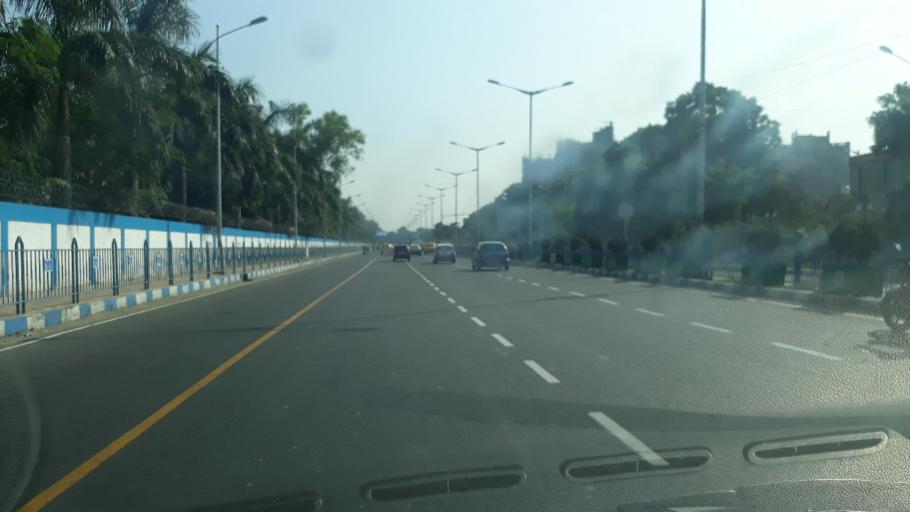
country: IN
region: West Bengal
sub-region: Kolkata
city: Kolkata
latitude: 22.5667
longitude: 88.4062
